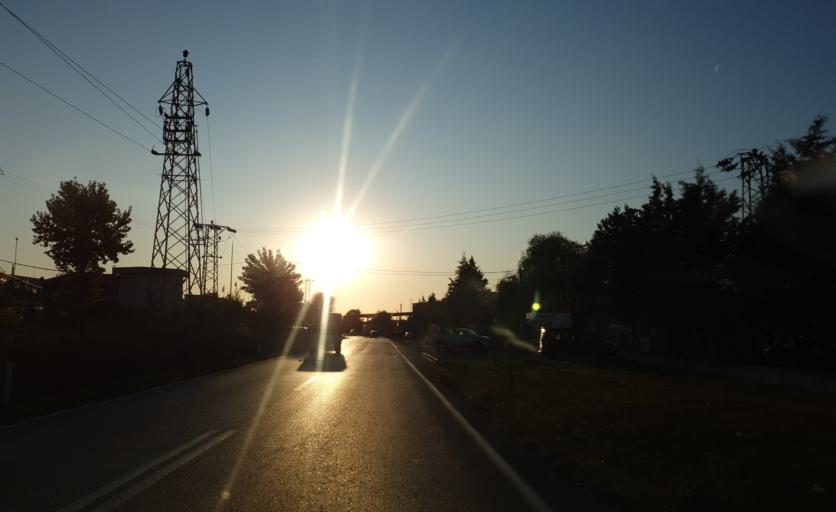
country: TR
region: Tekirdag
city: Beyazkoy
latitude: 41.3369
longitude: 27.7021
